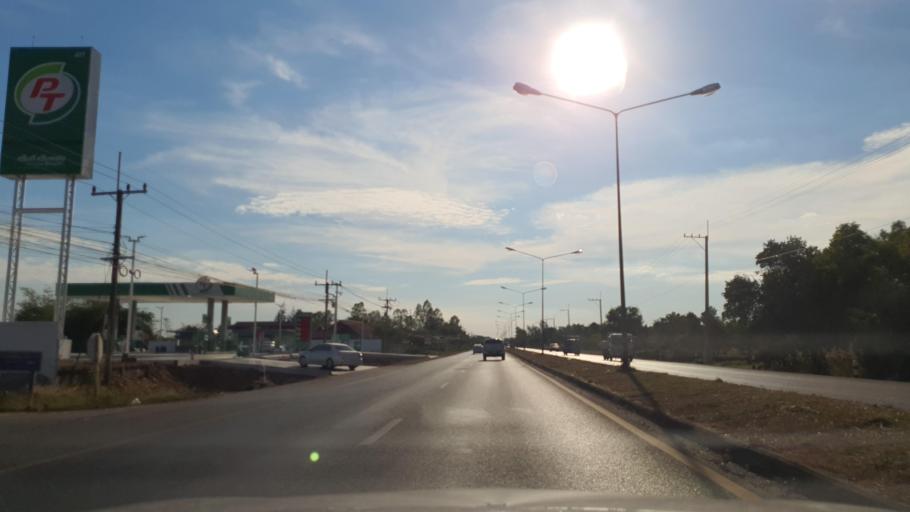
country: TH
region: Maha Sarakham
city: Kantharawichai
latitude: 16.3460
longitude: 103.3206
